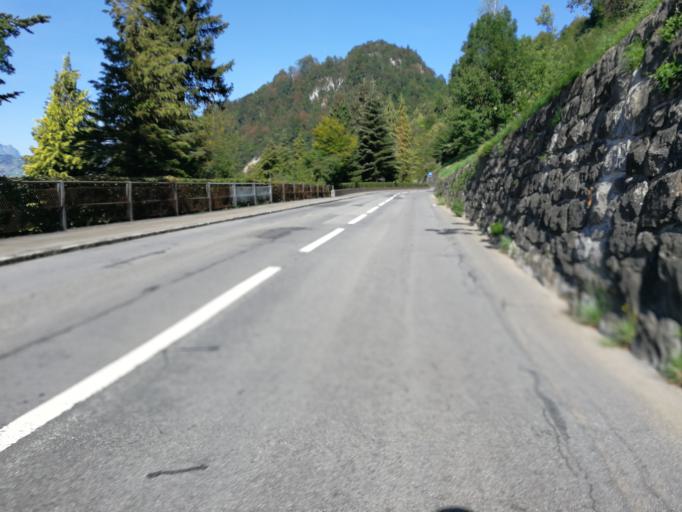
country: CH
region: Lucerne
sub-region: Lucerne-Land District
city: Vitznau
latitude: 46.9931
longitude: 8.4895
